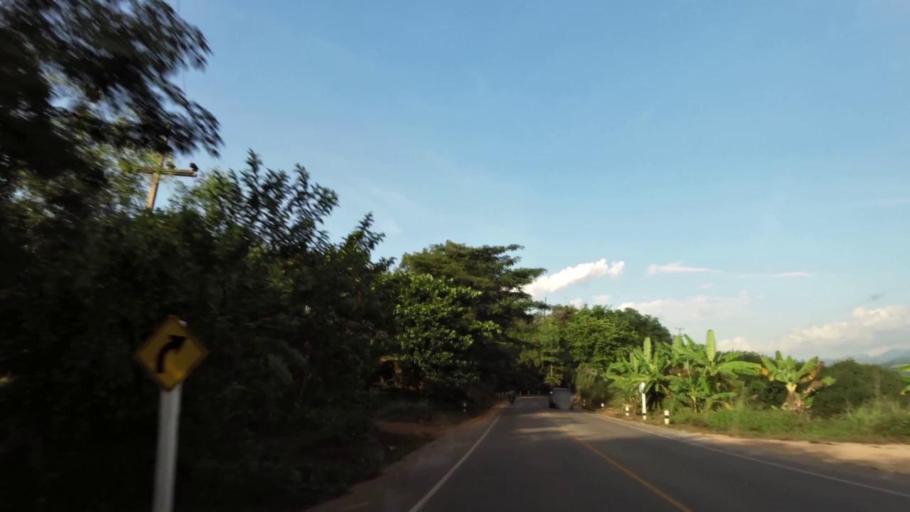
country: TH
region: Chiang Rai
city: Khun Tan
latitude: 19.8594
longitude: 100.3928
